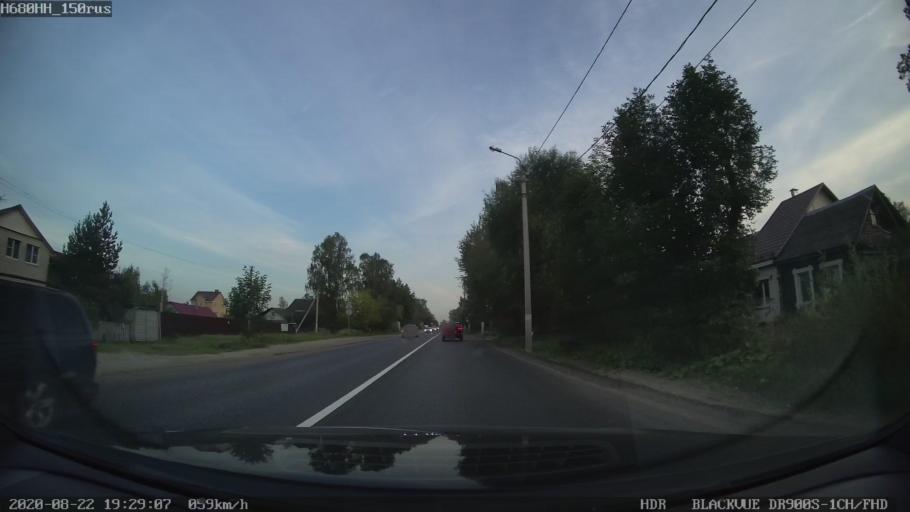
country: RU
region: Tverskaya
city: Tver
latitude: 56.8726
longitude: 35.9423
